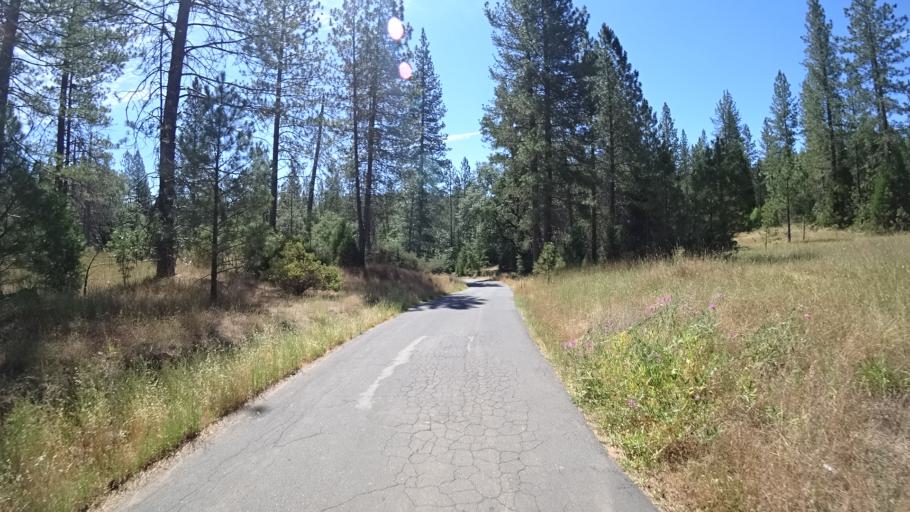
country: US
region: California
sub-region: Amador County
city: Pioneer
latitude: 38.3399
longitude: -120.5097
